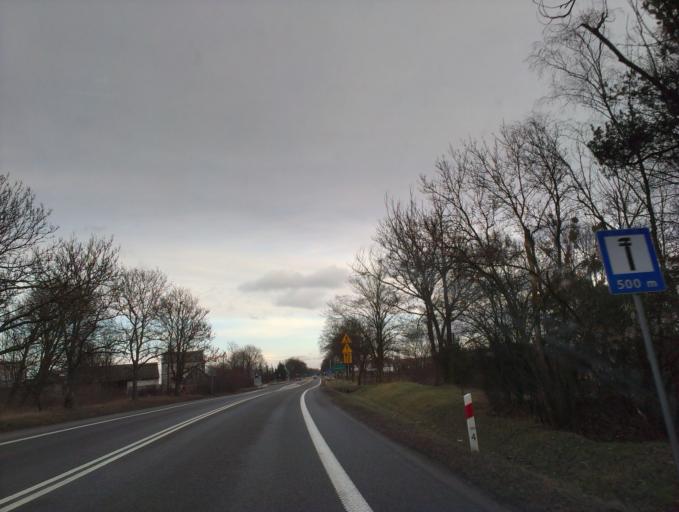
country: PL
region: Masovian Voivodeship
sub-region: Powiat sierpecki
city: Sierpc
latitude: 52.8709
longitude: 19.6431
